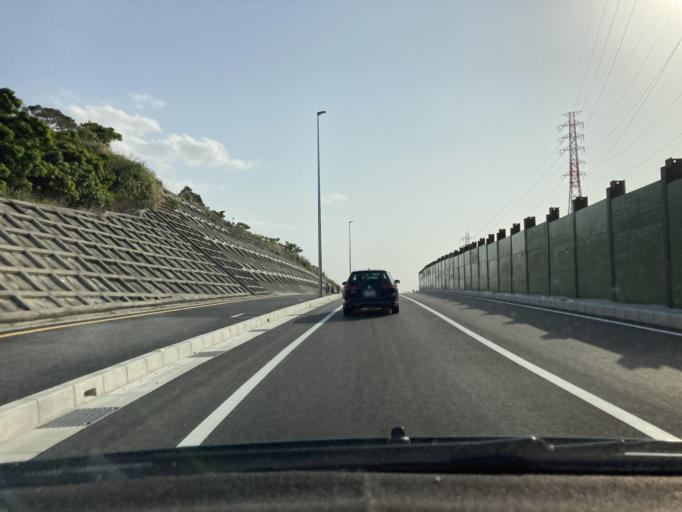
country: JP
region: Okinawa
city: Ginowan
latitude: 26.2064
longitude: 127.7508
